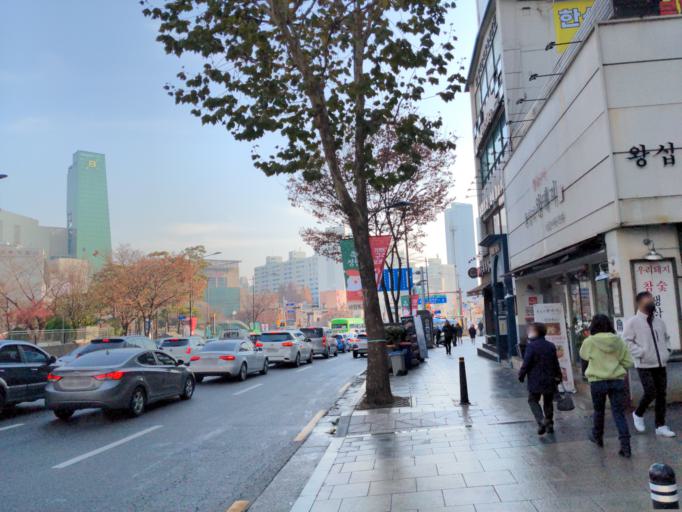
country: KR
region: Seoul
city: Seoul
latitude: 37.5619
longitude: 127.0344
